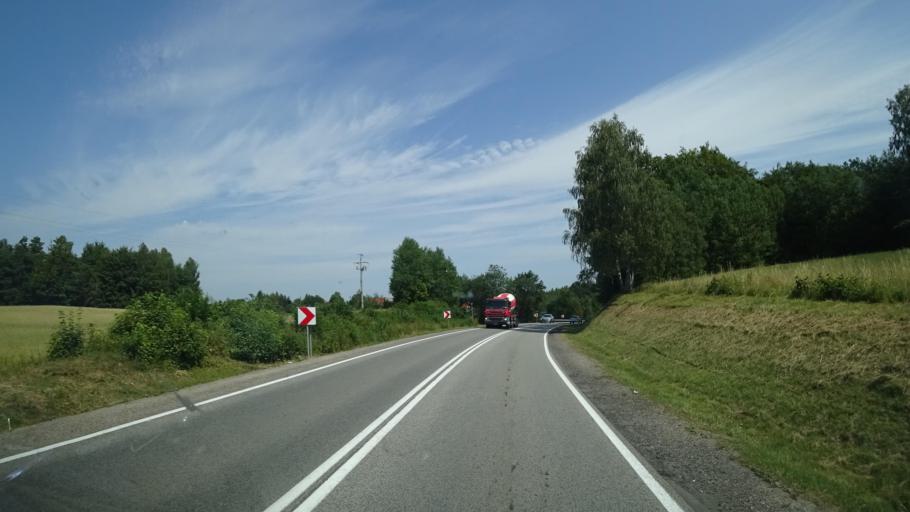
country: PL
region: Pomeranian Voivodeship
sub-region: Powiat koscierski
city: Grabowo Koscierskie
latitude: 54.2224
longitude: 18.1419
